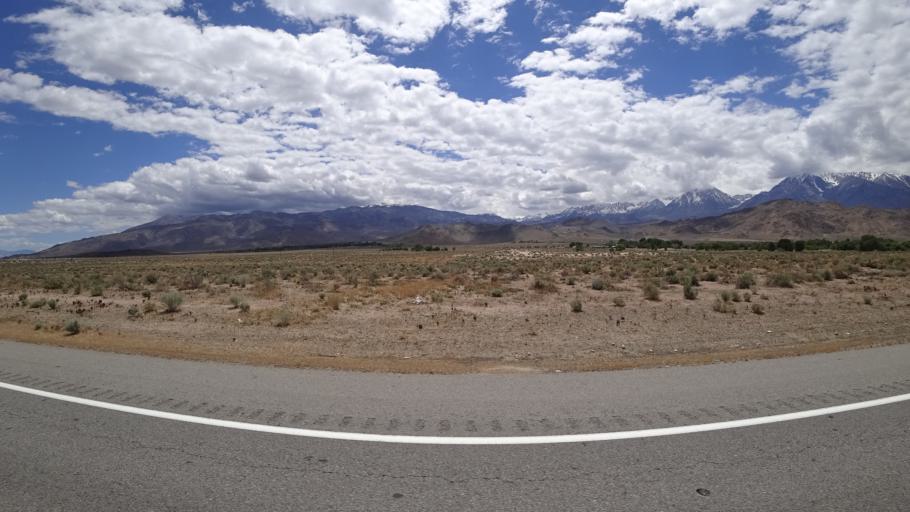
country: US
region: California
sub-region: Inyo County
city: West Bishop
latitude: 37.3824
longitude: -118.4817
